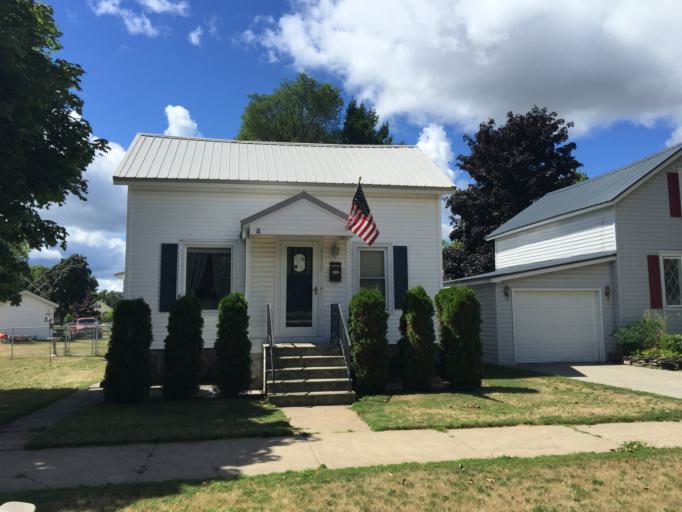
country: US
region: Wisconsin
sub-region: Marinette County
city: Marinette
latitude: 45.0931
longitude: -87.6204
